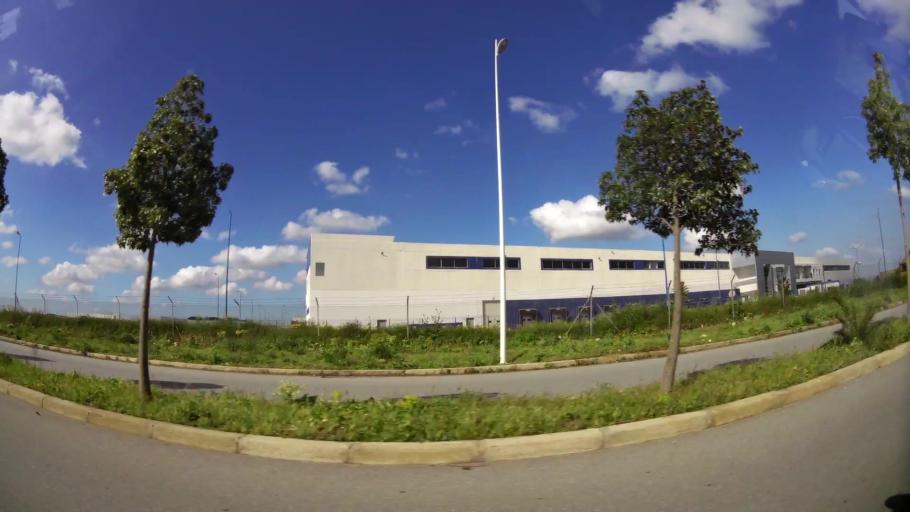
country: MA
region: Grand Casablanca
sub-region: Mediouna
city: Mediouna
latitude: 33.3891
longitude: -7.5399
